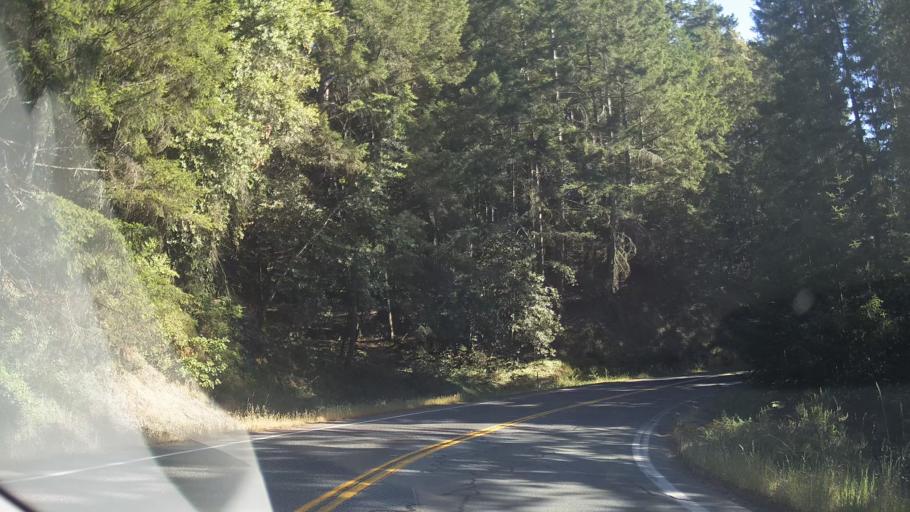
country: US
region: California
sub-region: Mendocino County
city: Brooktrails
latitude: 39.3961
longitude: -123.4536
